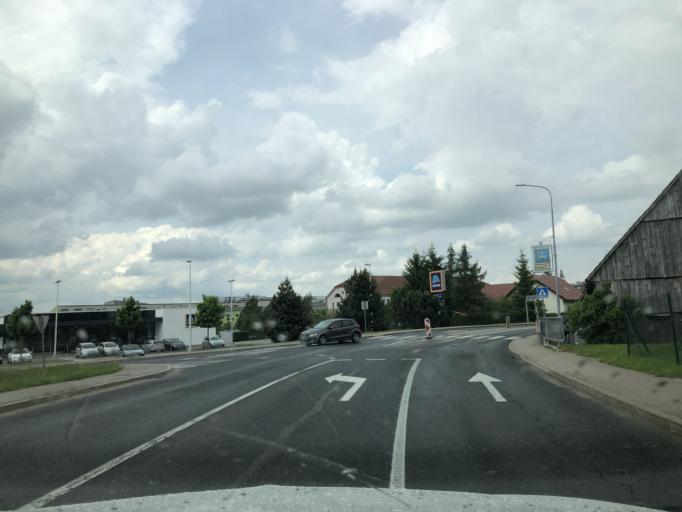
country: SI
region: Cerknica
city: Cerknica
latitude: 45.7901
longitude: 14.3675
